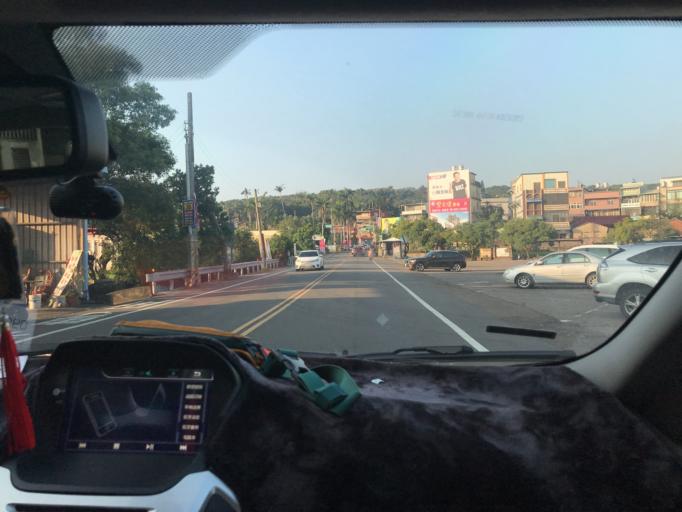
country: TW
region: Taiwan
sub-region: Hsinchu
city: Zhubei
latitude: 24.8417
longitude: 121.0366
